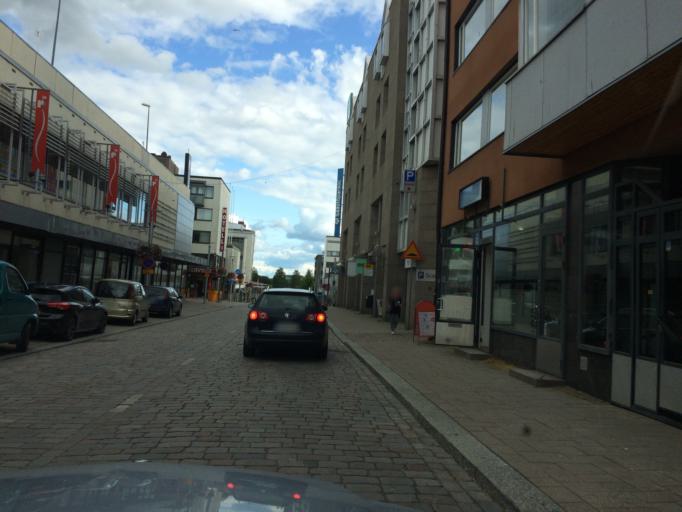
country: FI
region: Haeme
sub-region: Haemeenlinna
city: Haemeenlinna
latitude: 60.9961
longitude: 24.4617
